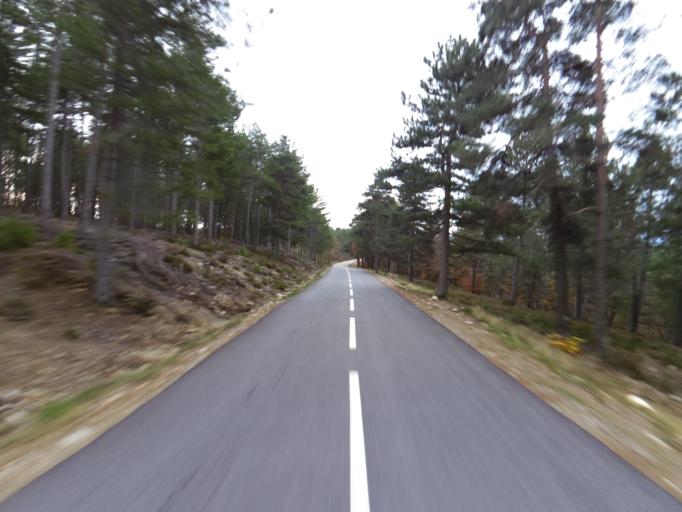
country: FR
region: Rhone-Alpes
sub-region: Departement de l'Ardeche
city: Les Vans
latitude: 44.4984
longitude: 4.1297
